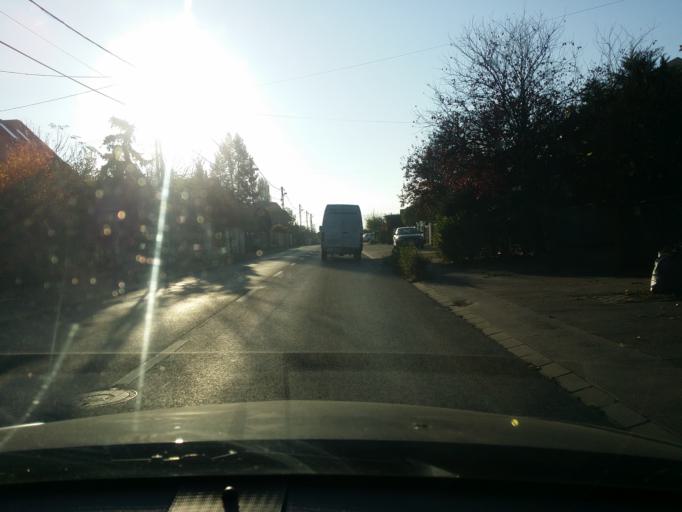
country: HU
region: Budapest
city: Budapest XVI. keruelet
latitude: 47.5185
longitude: 19.1699
